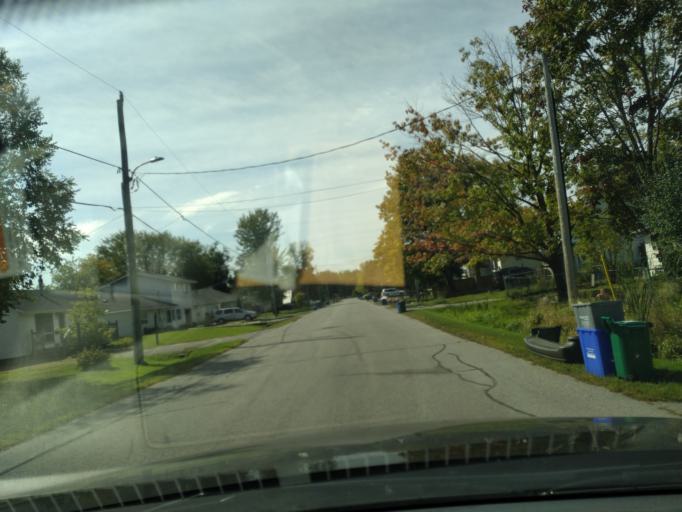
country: CA
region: Ontario
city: Keswick
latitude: 44.1981
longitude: -79.4763
